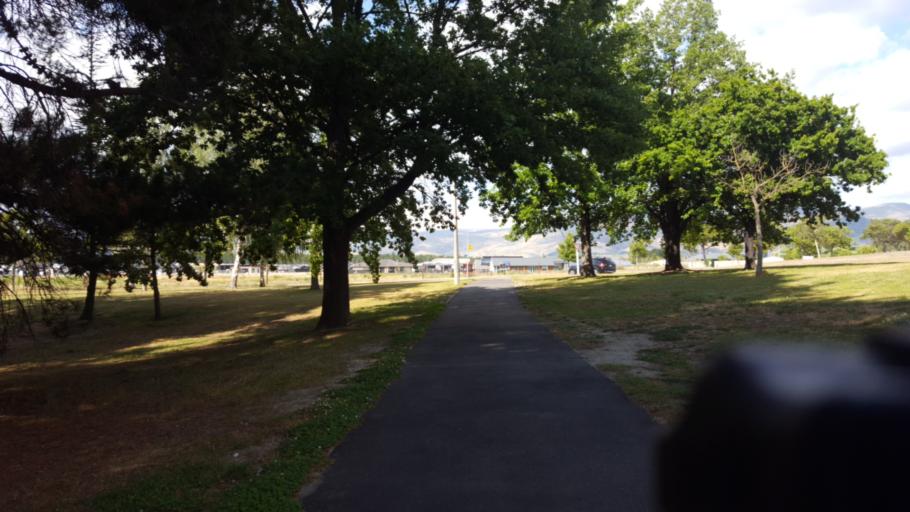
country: NZ
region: Otago
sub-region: Queenstown-Lakes District
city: Wanaka
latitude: -45.0445
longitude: 169.1904
